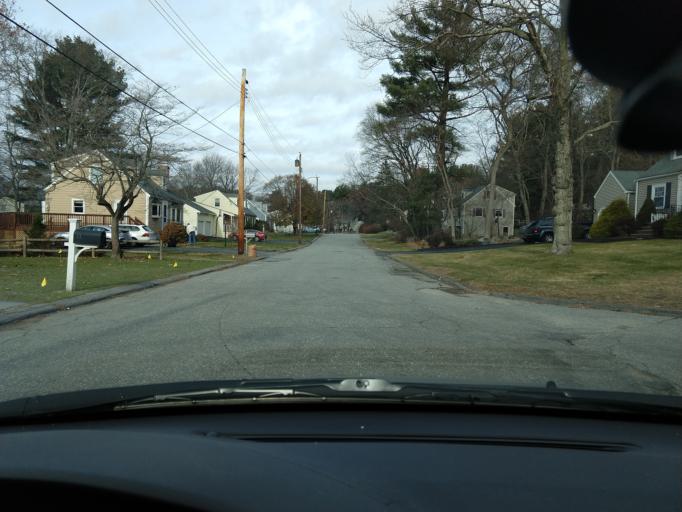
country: US
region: Massachusetts
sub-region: Middlesex County
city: Bedford
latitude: 42.4786
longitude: -71.2591
